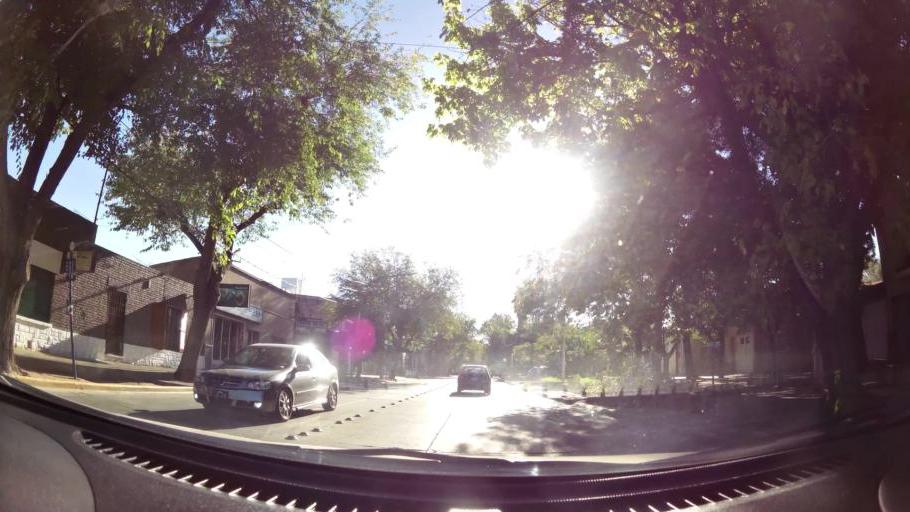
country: AR
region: Mendoza
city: Las Heras
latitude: -32.8668
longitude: -68.8304
